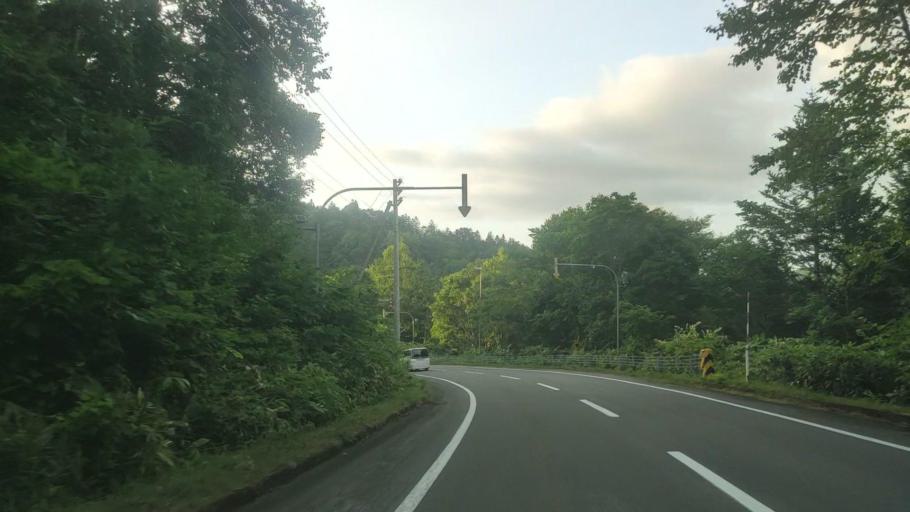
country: JP
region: Hokkaido
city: Bibai
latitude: 43.1797
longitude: 142.0664
